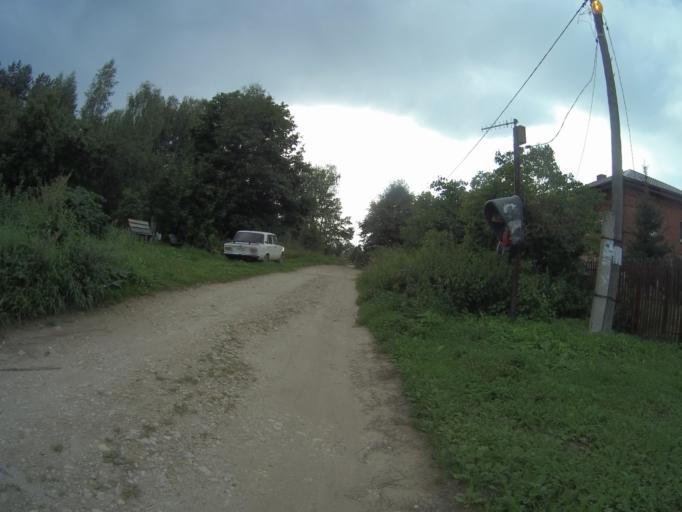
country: RU
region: Vladimir
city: Vorsha
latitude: 56.0227
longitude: 40.1886
